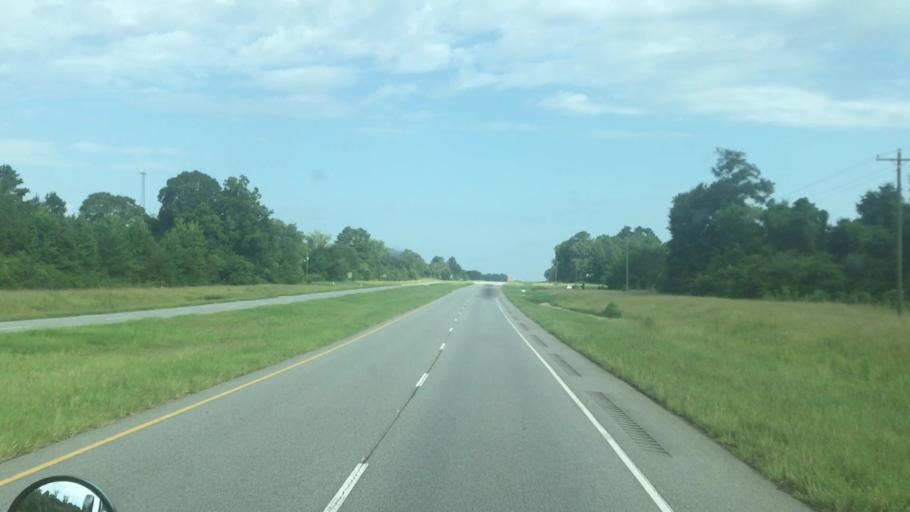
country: US
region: Georgia
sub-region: Early County
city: Blakely
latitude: 31.3412
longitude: -84.9057
